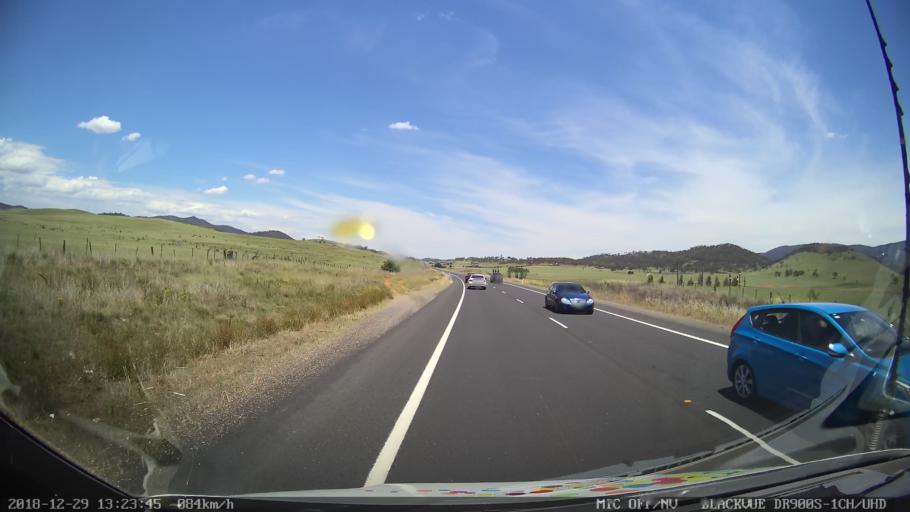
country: AU
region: Australian Capital Territory
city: Macarthur
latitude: -35.8208
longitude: 149.1633
